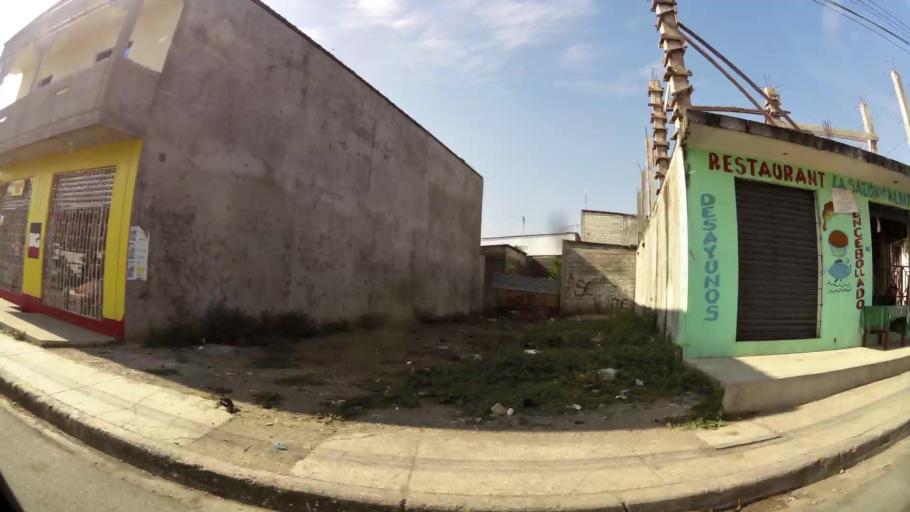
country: EC
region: Guayas
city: Eloy Alfaro
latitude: -2.0859
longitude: -79.9246
